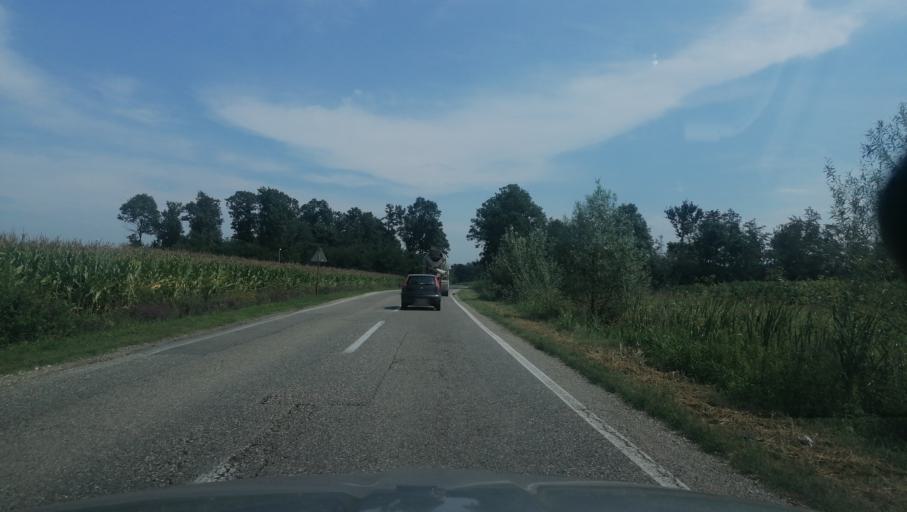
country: BA
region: Republika Srpska
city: Velika Obarska
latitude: 44.7803
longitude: 19.1023
